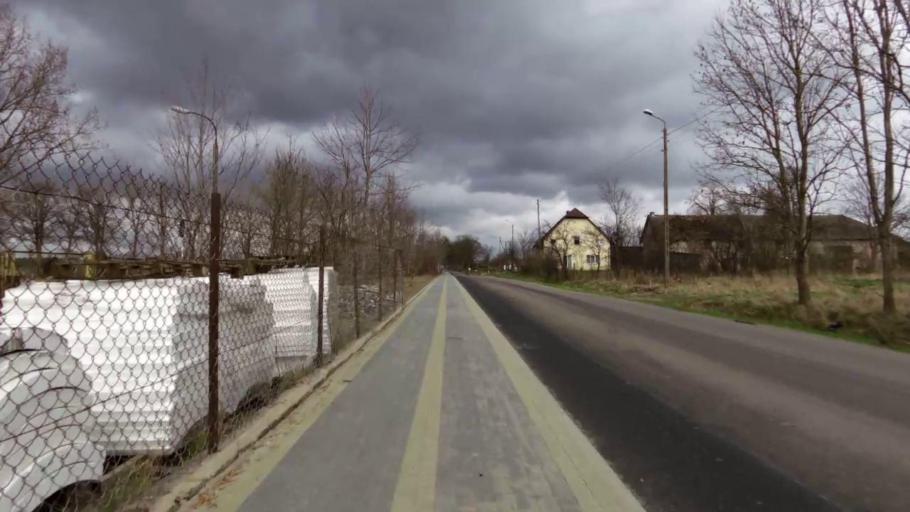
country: PL
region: West Pomeranian Voivodeship
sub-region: Powiat koszalinski
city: Sianow
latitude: 54.2445
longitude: 16.2986
